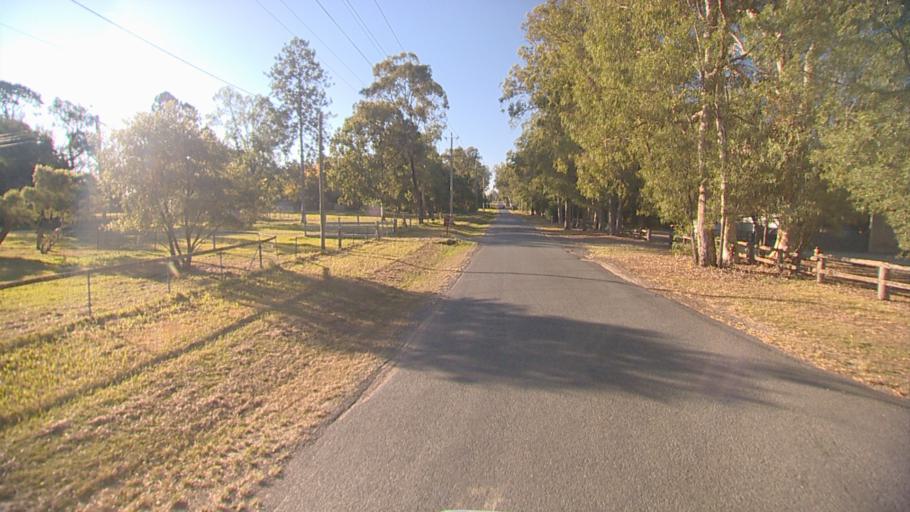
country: AU
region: Queensland
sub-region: Logan
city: Chambers Flat
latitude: -27.7833
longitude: 153.0868
